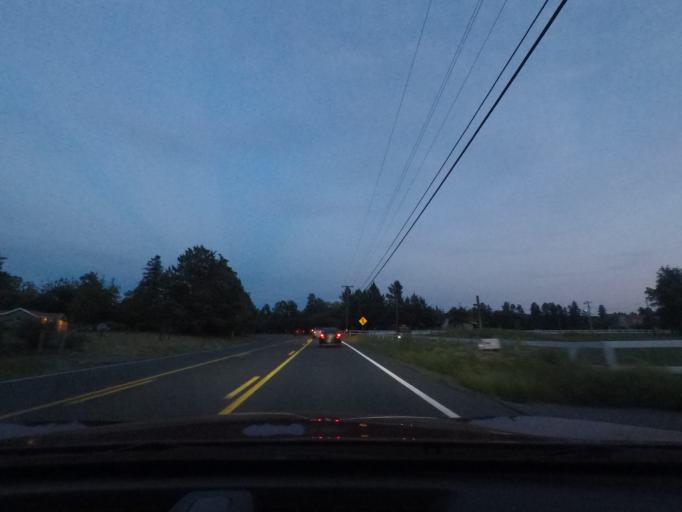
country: US
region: Arizona
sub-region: Yavapai County
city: Prescott
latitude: 34.5710
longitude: -112.5098
